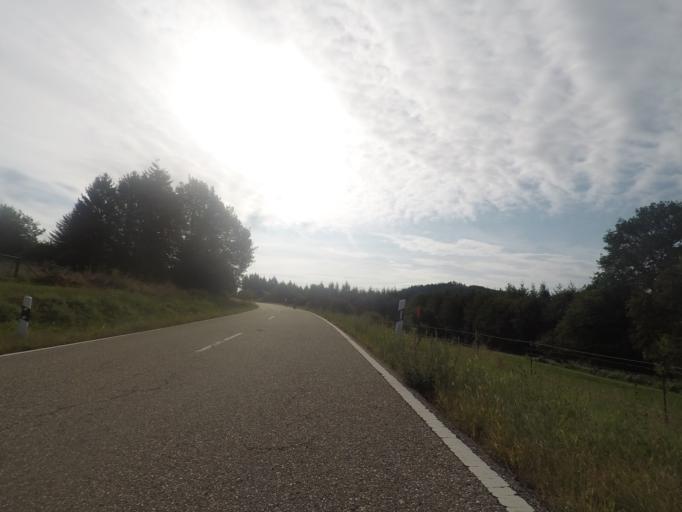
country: DE
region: Baden-Wuerttemberg
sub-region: Karlsruhe Region
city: Malsch
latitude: 48.8475
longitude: 8.3655
